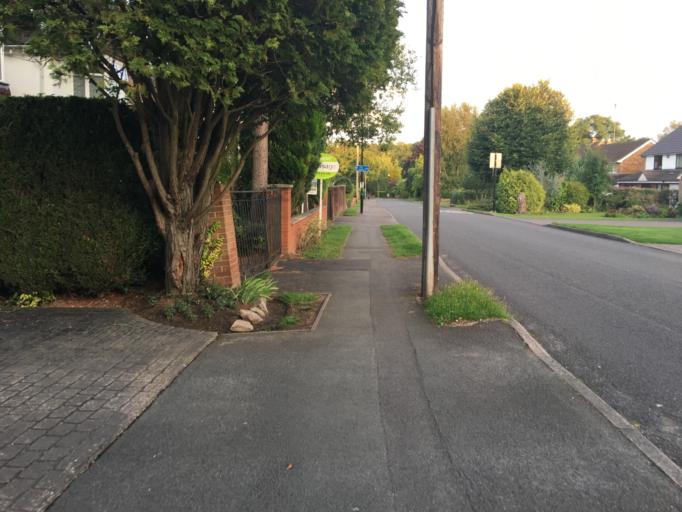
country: GB
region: England
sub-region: Coventry
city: Coventry
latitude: 52.3839
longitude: -1.5464
